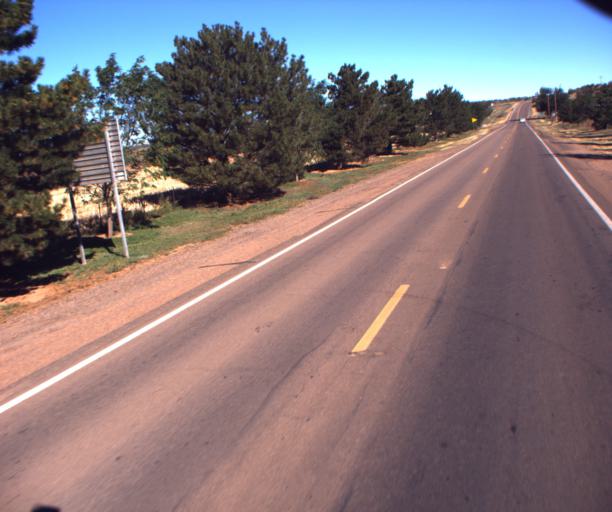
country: US
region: Arizona
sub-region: Navajo County
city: Snowflake
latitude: 34.5251
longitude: -110.0804
